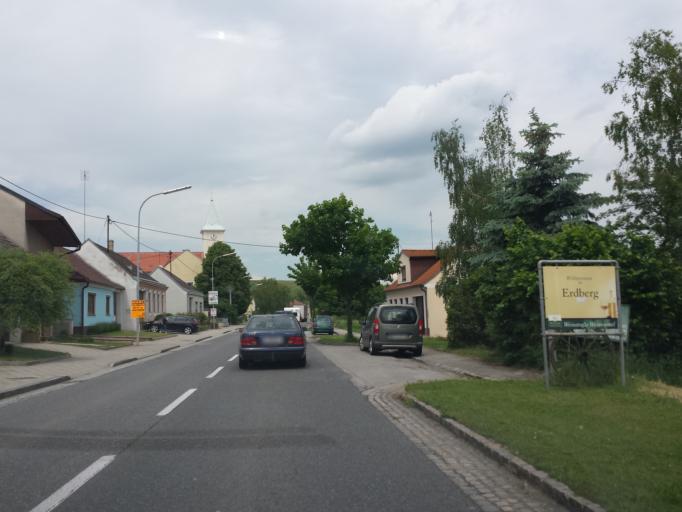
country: AT
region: Lower Austria
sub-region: Politischer Bezirk Mistelbach
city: Wilfersdorf
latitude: 48.6233
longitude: 16.6464
